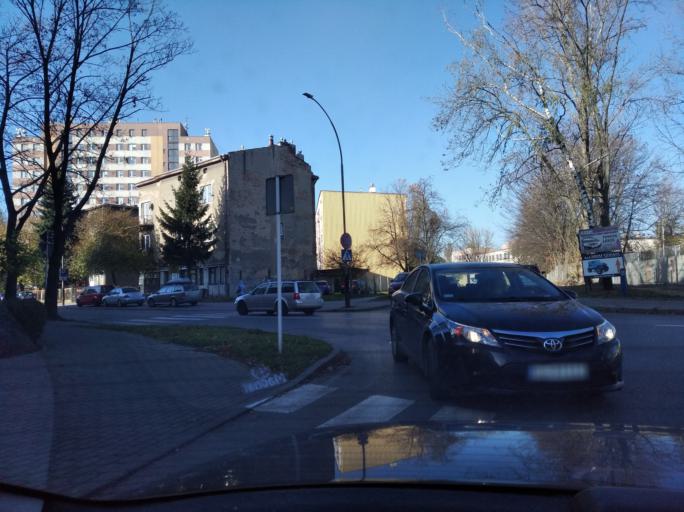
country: PL
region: Subcarpathian Voivodeship
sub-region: Rzeszow
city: Rzeszow
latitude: 50.0317
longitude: 21.9904
